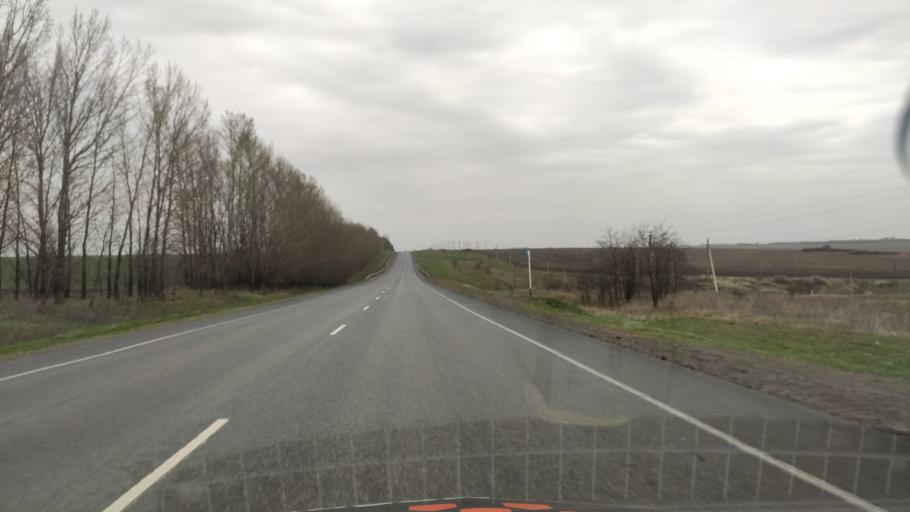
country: RU
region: Kursk
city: Gorshechnoye
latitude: 51.4991
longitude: 37.9817
